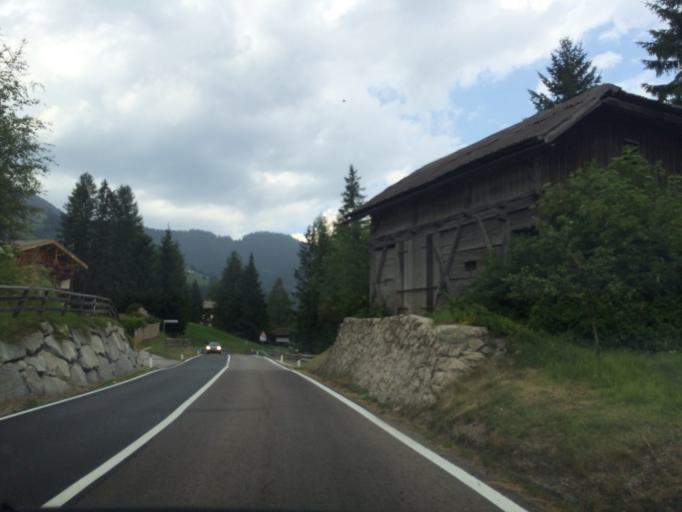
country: IT
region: Trentino-Alto Adige
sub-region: Bolzano
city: Badia
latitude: 46.6155
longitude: 11.8938
